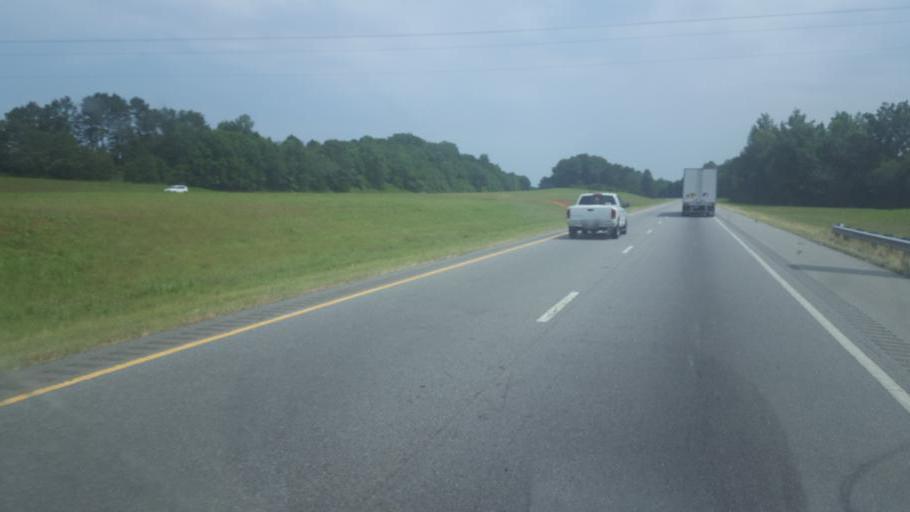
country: US
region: North Carolina
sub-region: Iredell County
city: Statesville
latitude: 35.9687
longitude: -80.8418
